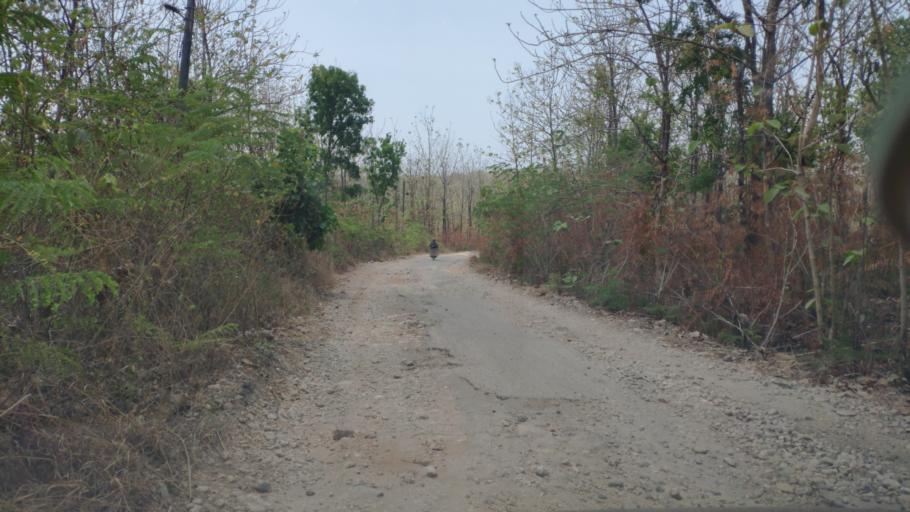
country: ID
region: Central Java
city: Randublatung
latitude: -7.2465
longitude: 111.3789
